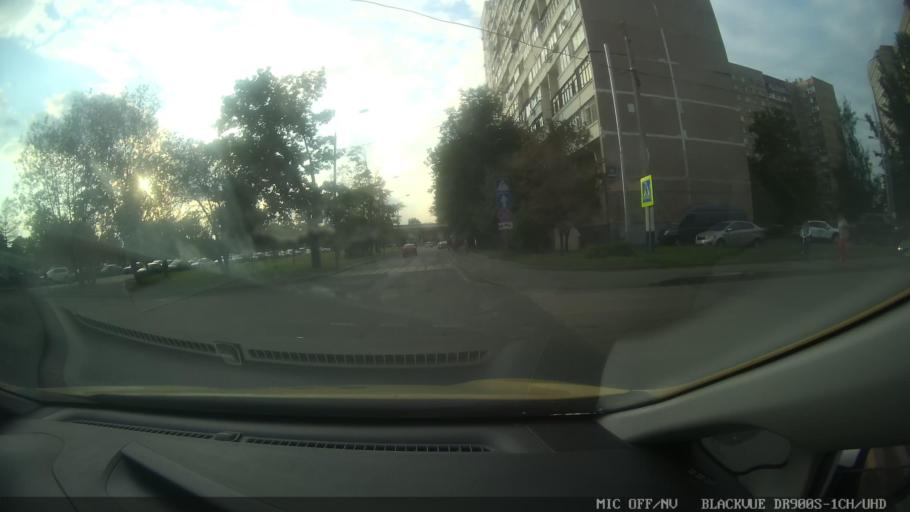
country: RU
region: Moscow
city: Vatutino
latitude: 55.8598
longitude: 37.6943
